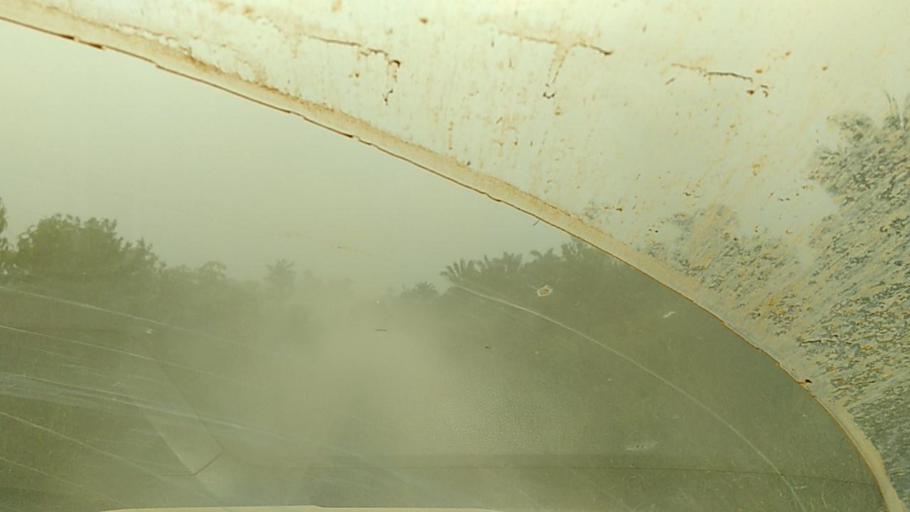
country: BR
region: Rondonia
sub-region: Porto Velho
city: Porto Velho
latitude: -8.7731
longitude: -63.1761
